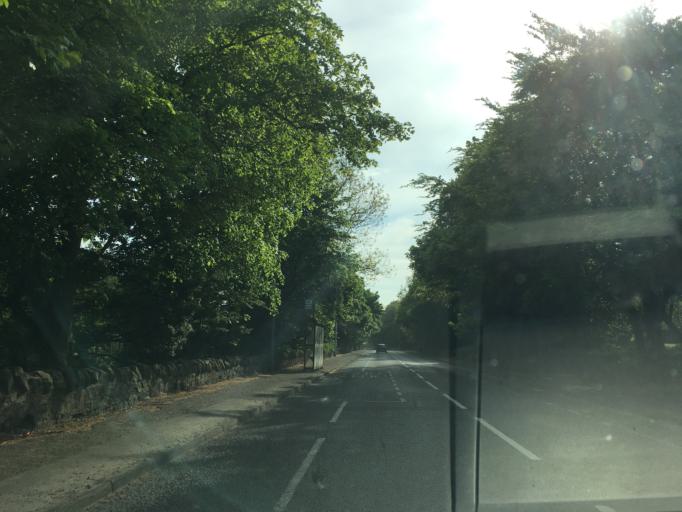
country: GB
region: Scotland
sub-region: Midlothian
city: Penicuik
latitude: 55.8434
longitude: -3.2071
